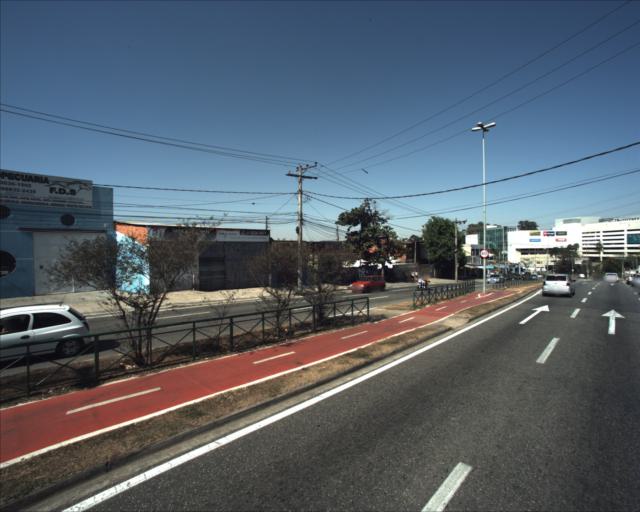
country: BR
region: Sao Paulo
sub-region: Sorocaba
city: Sorocaba
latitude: -23.4533
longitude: -47.4827
